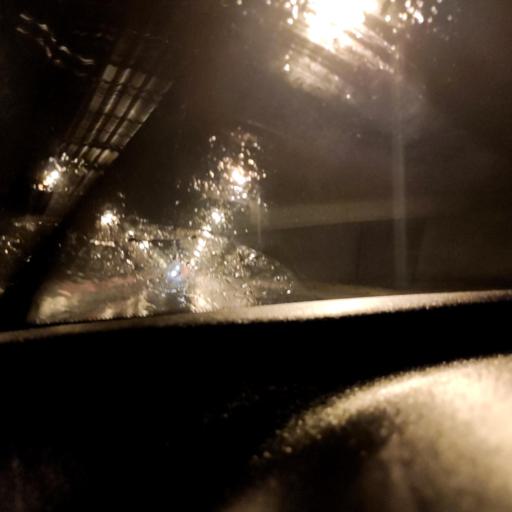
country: RU
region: Samara
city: Novosemeykino
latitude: 53.3377
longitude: 50.2323
